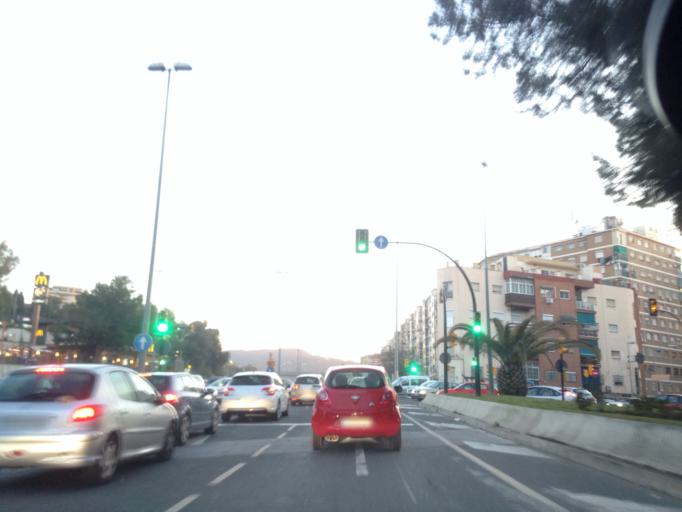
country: ES
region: Andalusia
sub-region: Provincia de Malaga
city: Malaga
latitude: 36.7291
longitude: -4.4447
